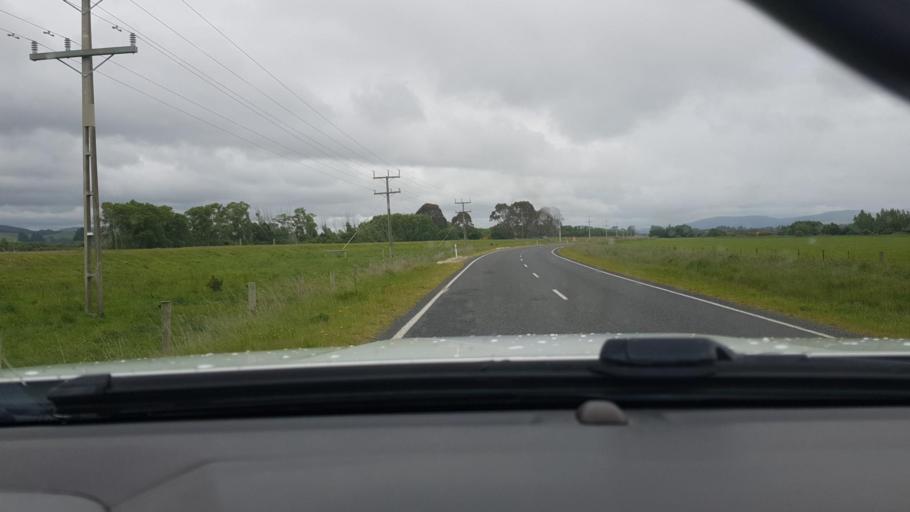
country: NZ
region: Southland
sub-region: Southland District
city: Winton
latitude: -45.8382
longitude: 168.3693
